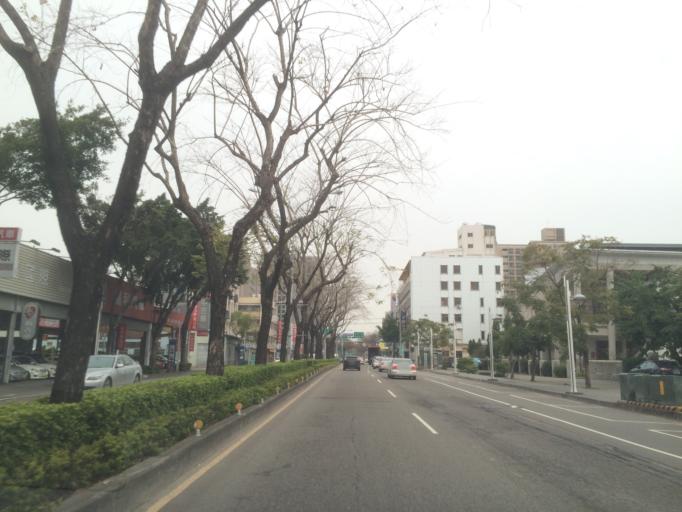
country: TW
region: Taiwan
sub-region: Taichung City
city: Taichung
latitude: 24.1920
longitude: 120.6865
